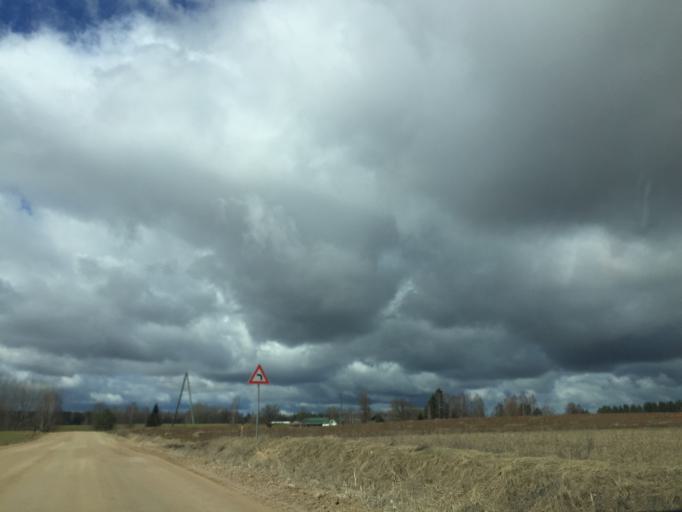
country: LV
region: Akniste
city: Akniste
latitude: 56.1064
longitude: 25.9497
